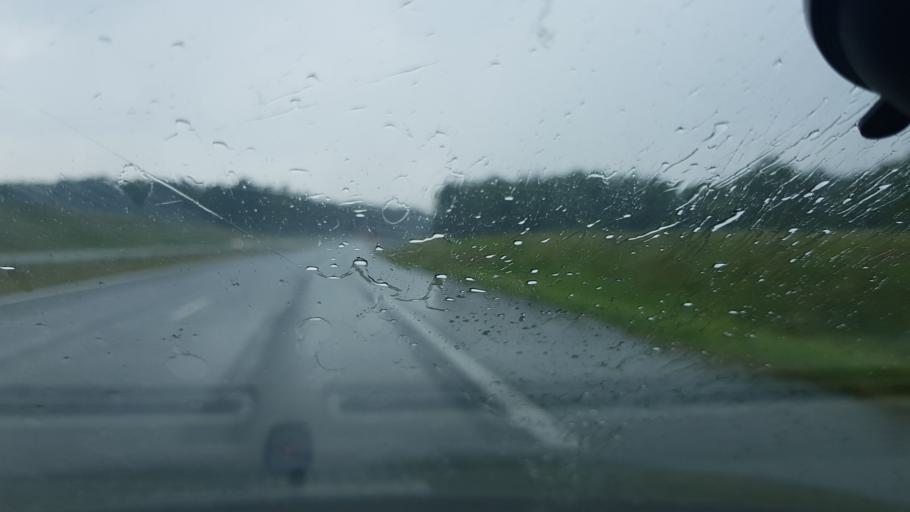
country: PL
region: Warmian-Masurian Voivodeship
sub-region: Powiat olsztynski
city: Olsztynek
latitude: 53.4520
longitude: 20.3232
